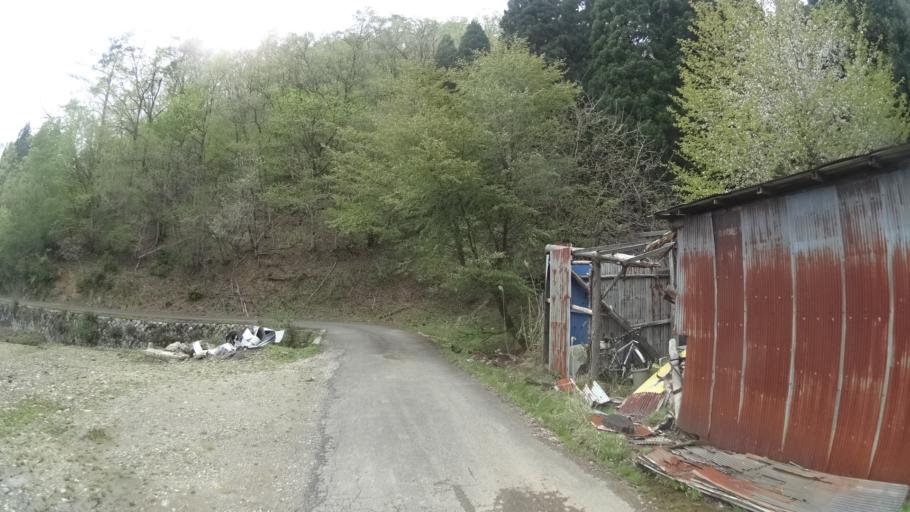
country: JP
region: Kyoto
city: Maizuru
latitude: 35.4012
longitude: 135.4967
